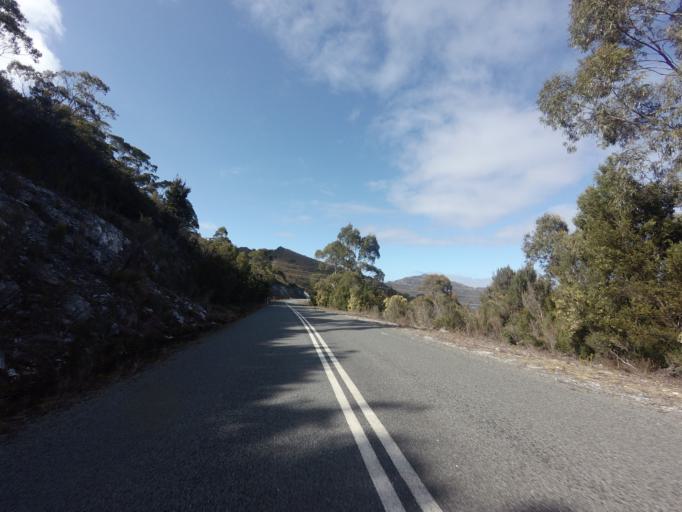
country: AU
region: Tasmania
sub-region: Huon Valley
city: Geeveston
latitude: -42.8266
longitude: 146.1254
